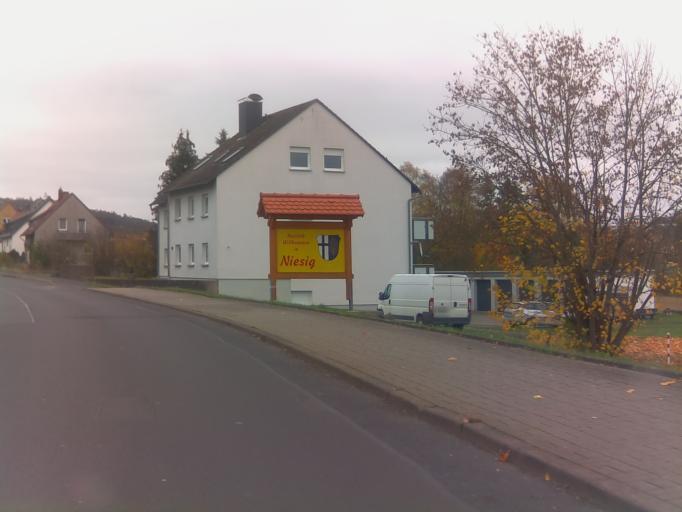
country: DE
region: Hesse
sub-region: Regierungsbezirk Kassel
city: Fulda
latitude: 50.5713
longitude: 9.6713
